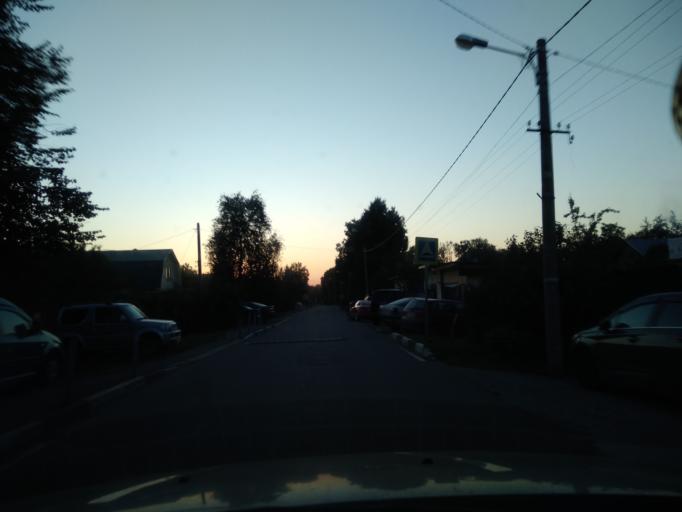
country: RU
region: Moscow
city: Strogino
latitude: 55.8619
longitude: 37.3904
